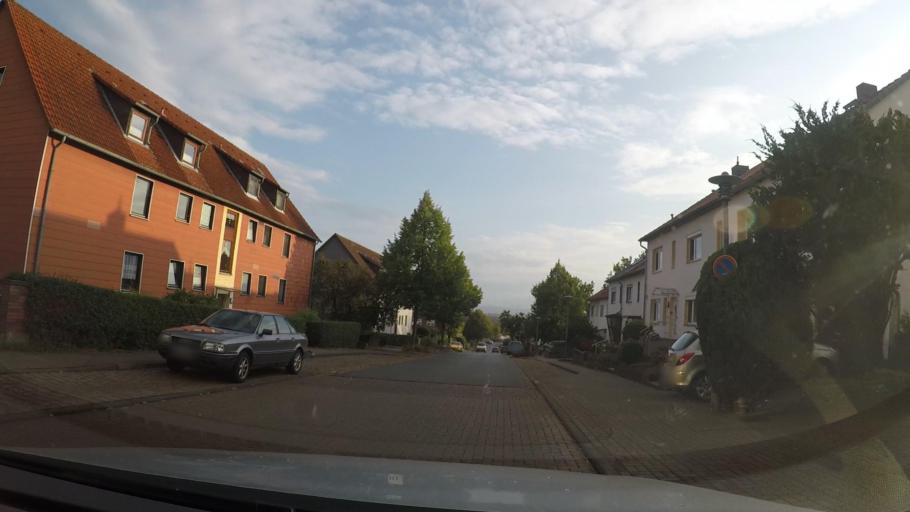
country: DE
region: Lower Saxony
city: Schoningen
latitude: 52.1333
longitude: 10.9586
